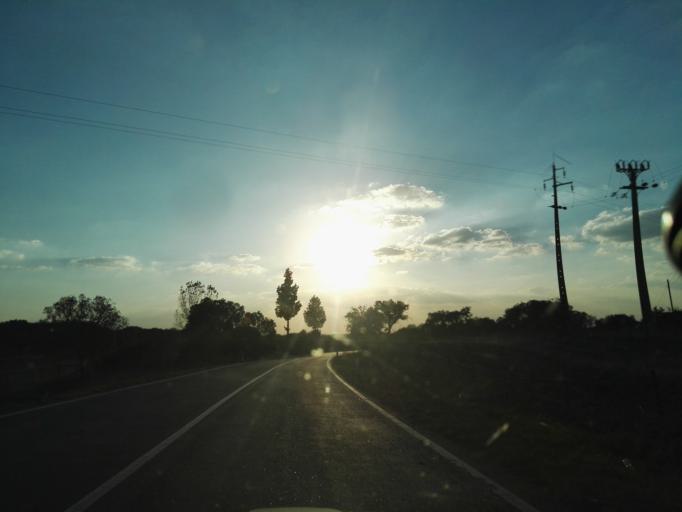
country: PT
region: Evora
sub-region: Mora
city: Mora
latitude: 38.8952
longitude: -8.0290
